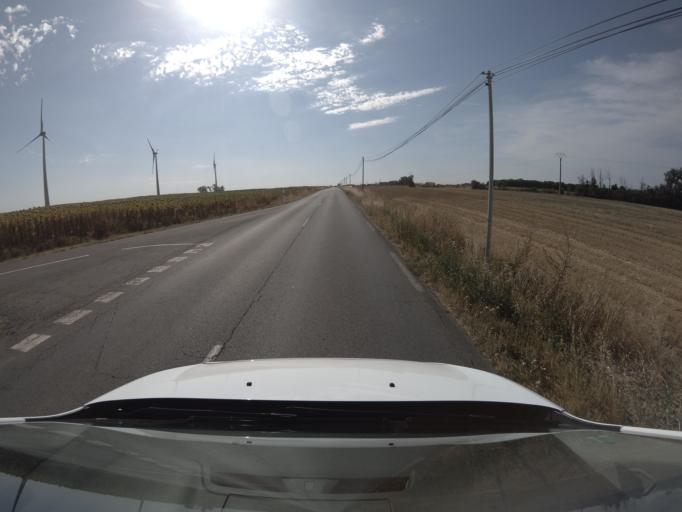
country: FR
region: Poitou-Charentes
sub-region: Departement des Deux-Sevres
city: Mauze-Thouarsais
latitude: 46.9986
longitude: -0.2746
